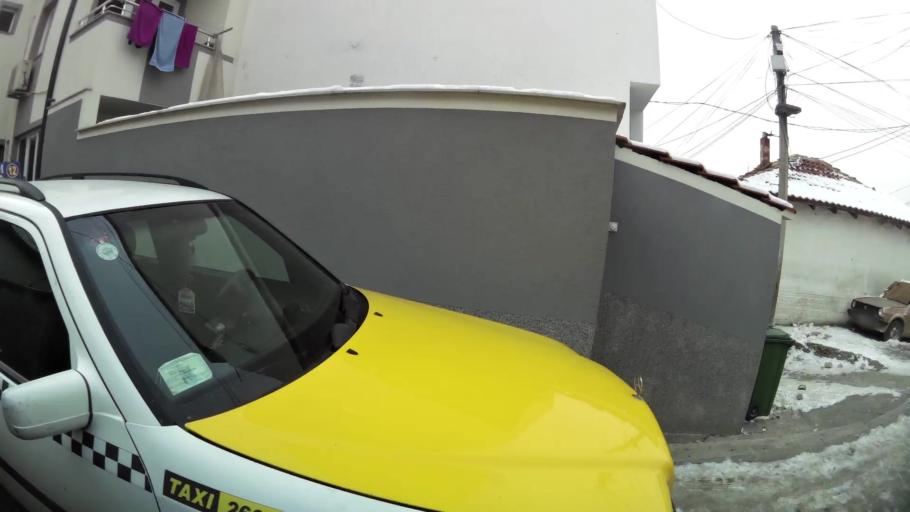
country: MK
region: Cair
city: Cair
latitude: 42.0042
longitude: 21.4469
